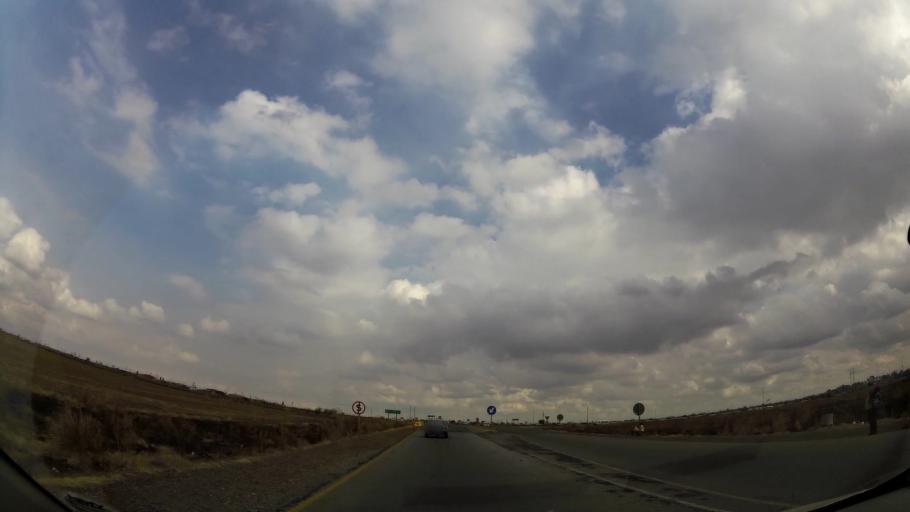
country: ZA
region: Orange Free State
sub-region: Fezile Dabi District Municipality
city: Sasolburg
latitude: -26.8454
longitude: 27.8904
